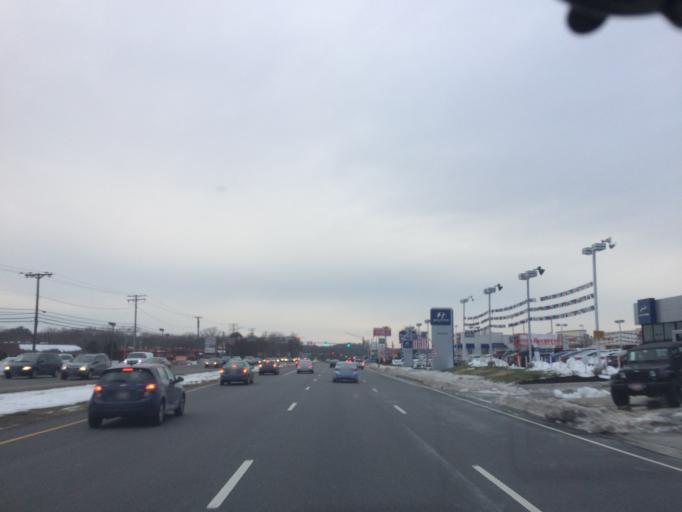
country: US
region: Maryland
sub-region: Baltimore County
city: Catonsville
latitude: 39.2851
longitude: -76.7598
